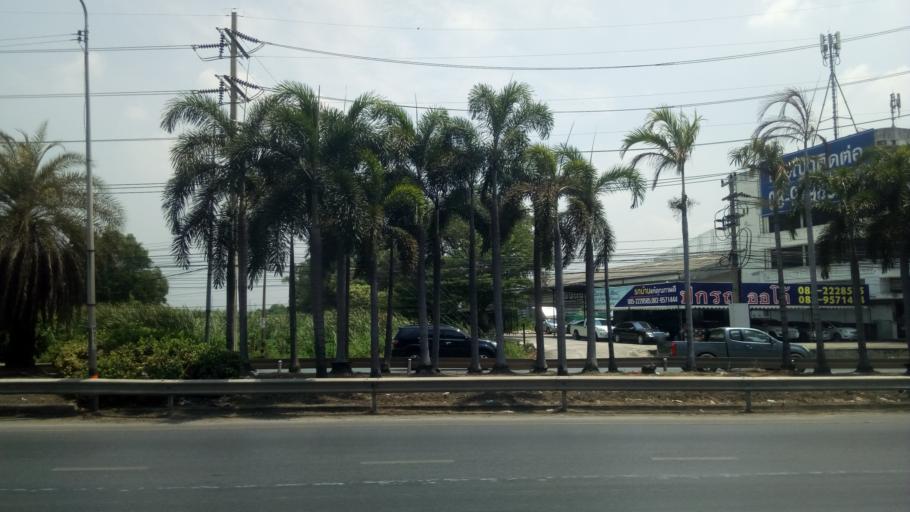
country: TH
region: Phra Nakhon Si Ayutthaya
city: Ban Bang Kadi Pathum Thani
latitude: 13.9851
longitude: 100.5884
